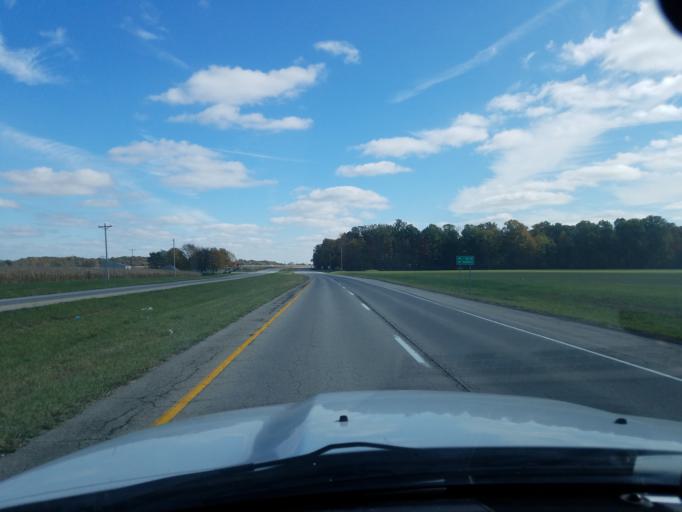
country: US
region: Indiana
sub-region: Ripley County
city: Milan
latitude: 39.0512
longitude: -85.1345
